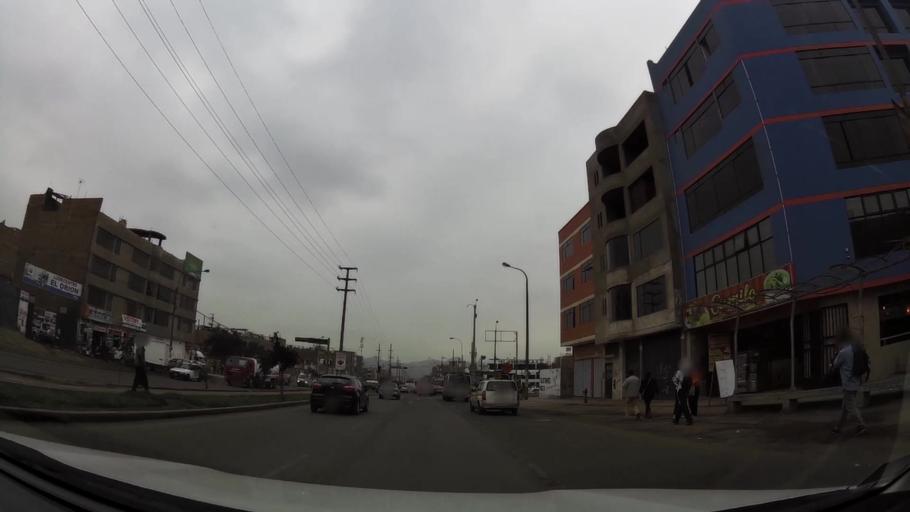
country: PE
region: Lima
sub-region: Lima
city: Vitarte
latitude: -12.0375
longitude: -76.9535
